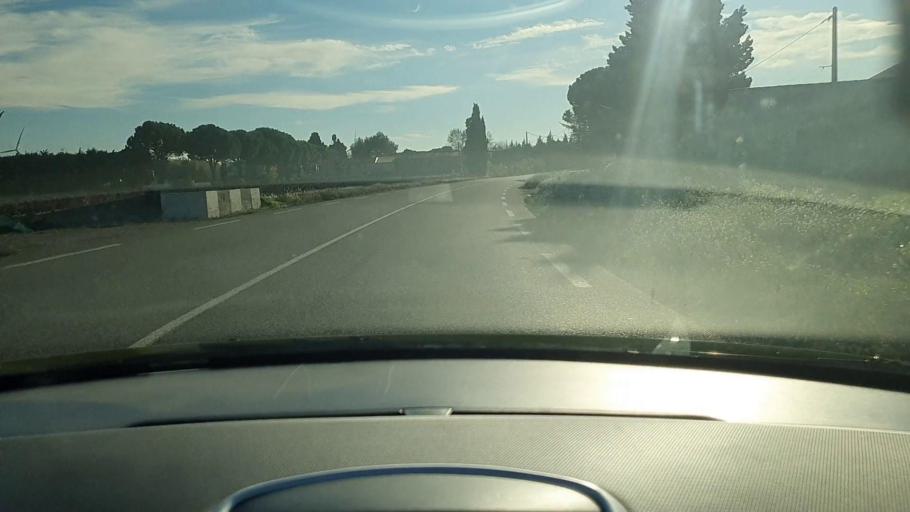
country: FR
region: Languedoc-Roussillon
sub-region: Departement du Gard
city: Beaucaire
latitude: 43.7871
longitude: 4.6276
